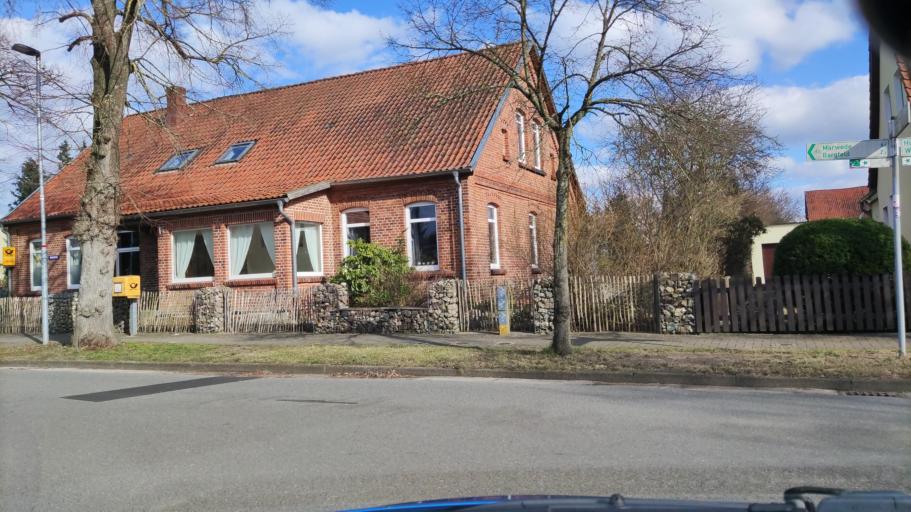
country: DE
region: Lower Saxony
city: Eldingen
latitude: 52.6836
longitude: 10.3447
